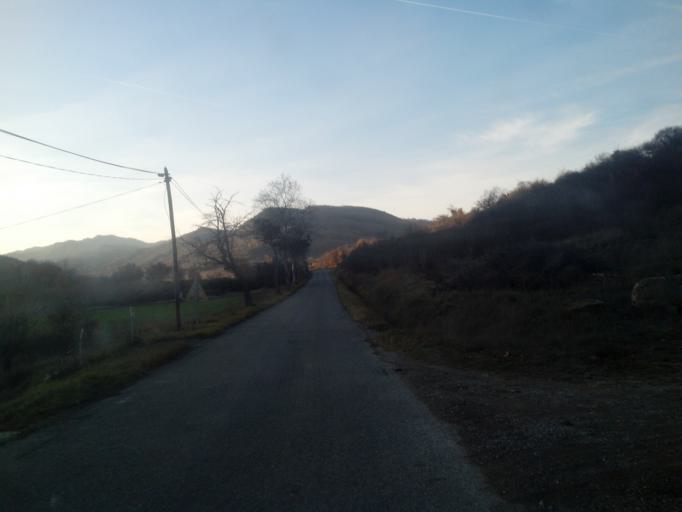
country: FR
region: Languedoc-Roussillon
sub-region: Departement de l'Aude
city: Esperaza
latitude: 42.9410
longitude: 2.1873
